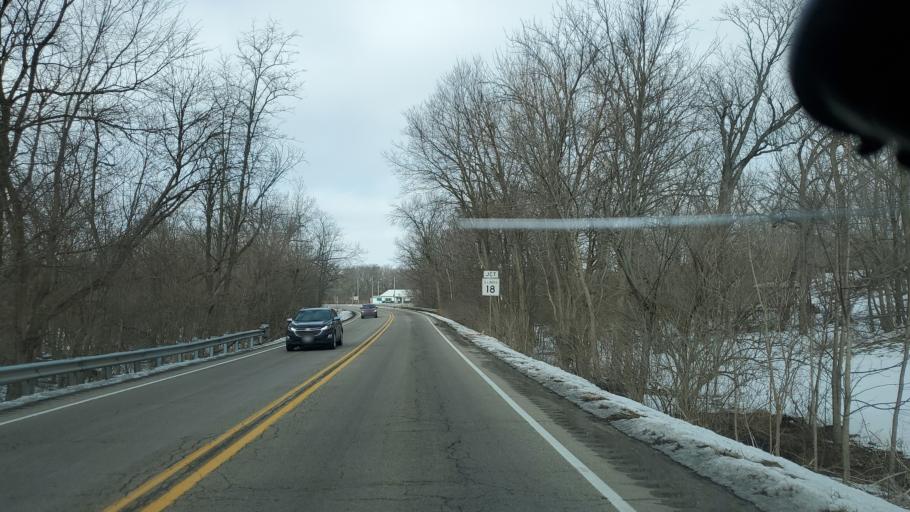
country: US
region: Illinois
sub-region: Marshall County
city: Toluca
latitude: 41.1162
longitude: -89.2013
